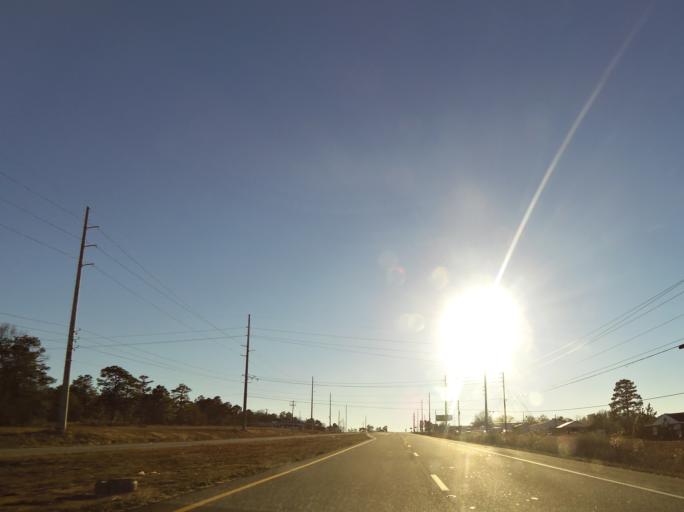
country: US
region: Georgia
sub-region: Houston County
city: Centerville
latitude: 32.6791
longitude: -83.7029
